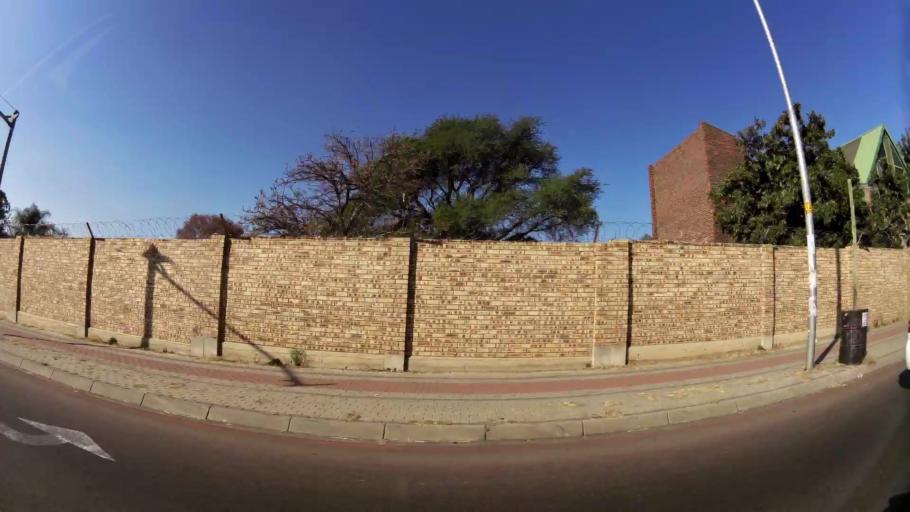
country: ZA
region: Gauteng
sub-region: City of Tshwane Metropolitan Municipality
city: Pretoria
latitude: -25.7386
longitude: 28.1874
